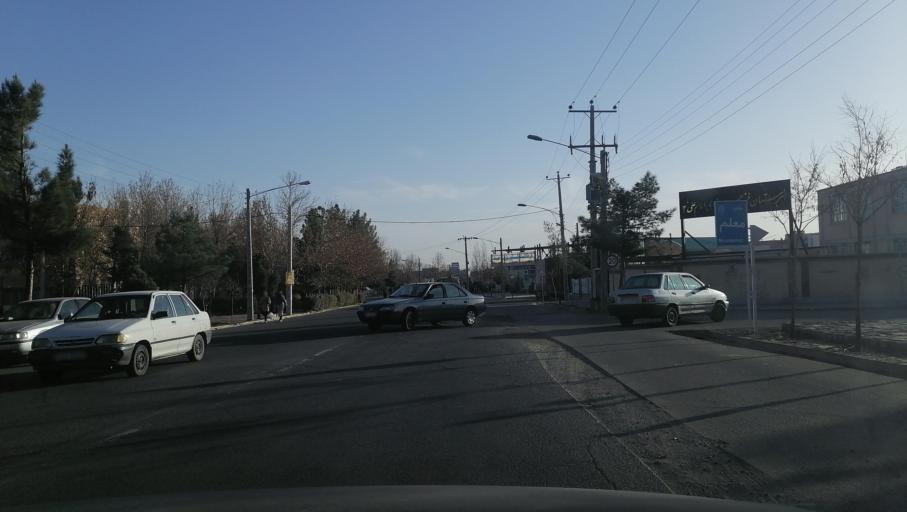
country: IR
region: Razavi Khorasan
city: Sabzevar
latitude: 36.2792
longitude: 57.6754
